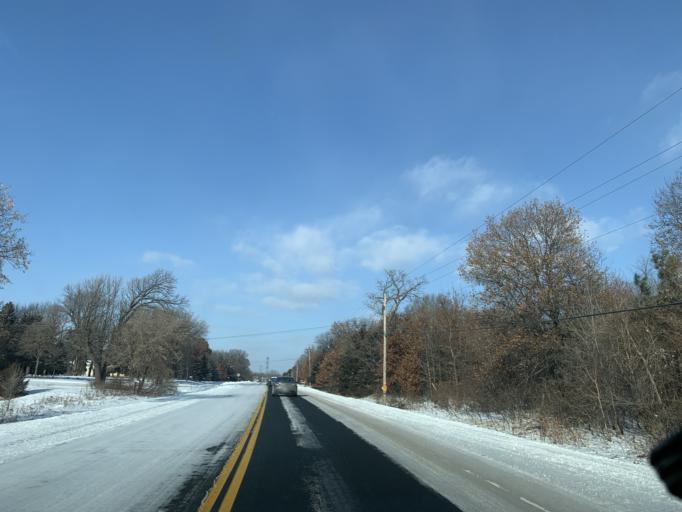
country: US
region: Minnesota
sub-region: Scott County
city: Prior Lake
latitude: 44.7689
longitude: -93.4047
